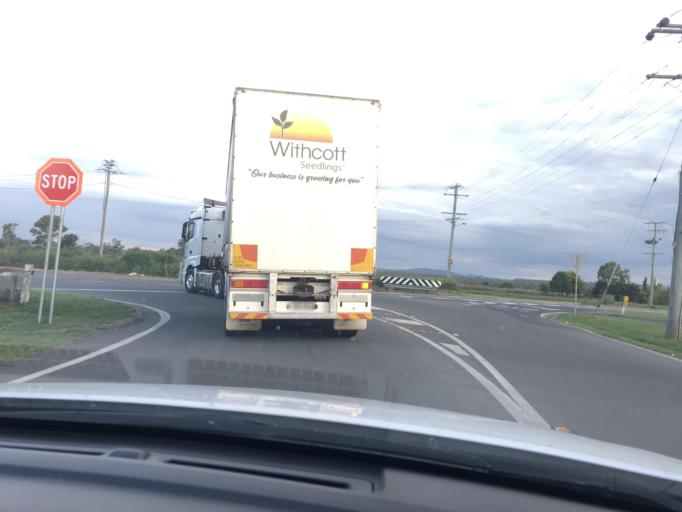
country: AU
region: Queensland
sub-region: Lockyer Valley
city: Gatton
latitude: -27.5836
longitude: 152.3634
